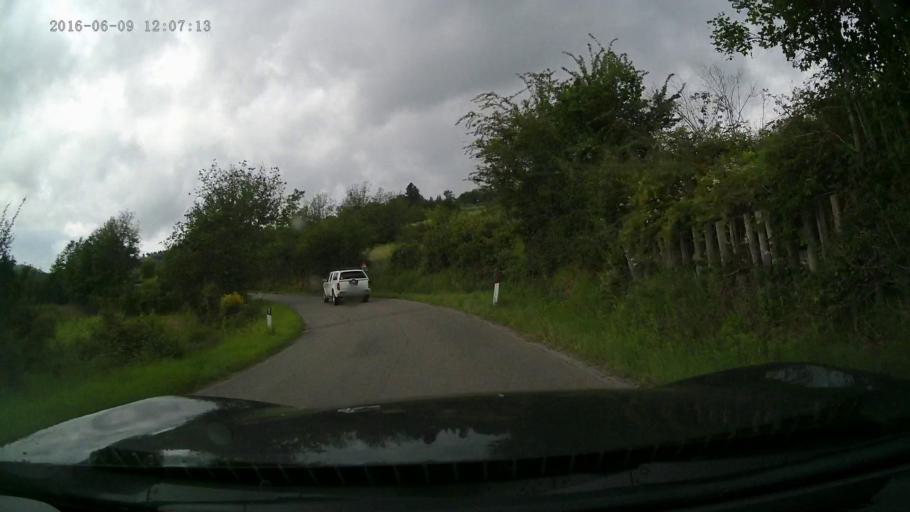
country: IT
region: Tuscany
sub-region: Province of Florence
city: Panzano in Chianti
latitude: 43.5277
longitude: 11.2854
